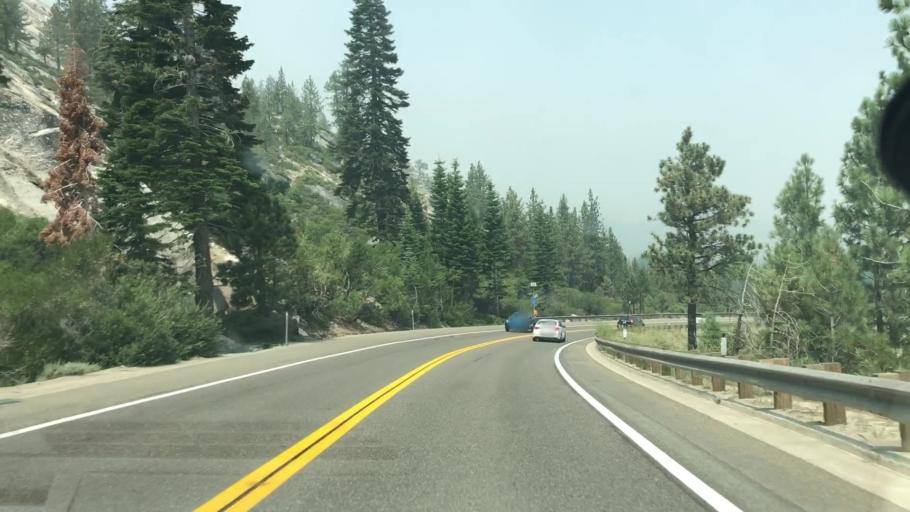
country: US
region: California
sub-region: El Dorado County
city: South Lake Tahoe
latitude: 38.8406
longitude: -120.0425
